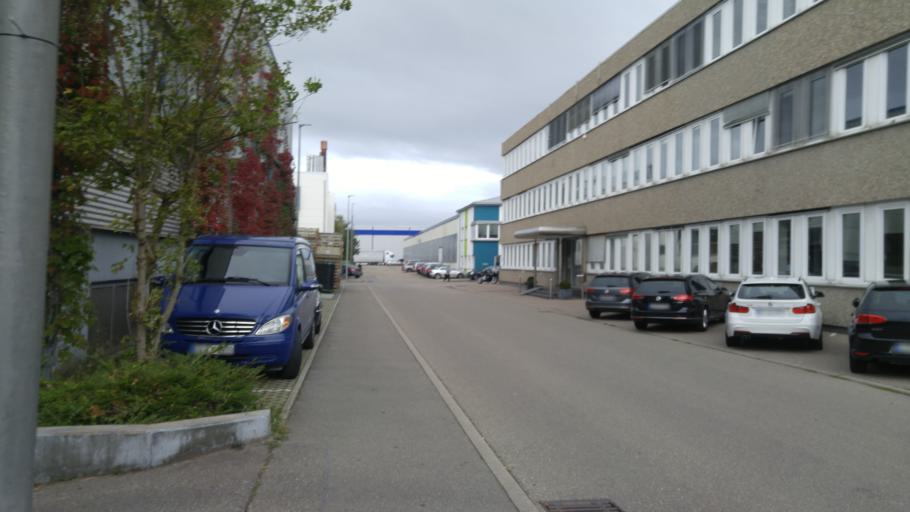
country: DE
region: Baden-Wuerttemberg
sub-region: Regierungsbezirk Stuttgart
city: Leonberg
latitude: 48.7960
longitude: 9.0032
